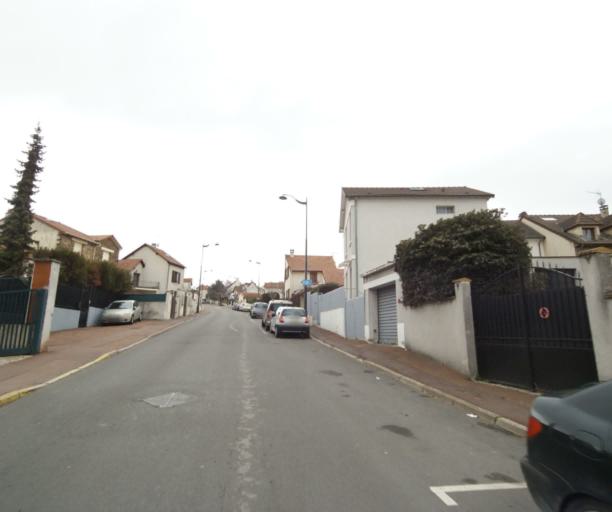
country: FR
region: Ile-de-France
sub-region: Departement des Hauts-de-Seine
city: Rueil-Malmaison
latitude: 48.8783
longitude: 2.1939
